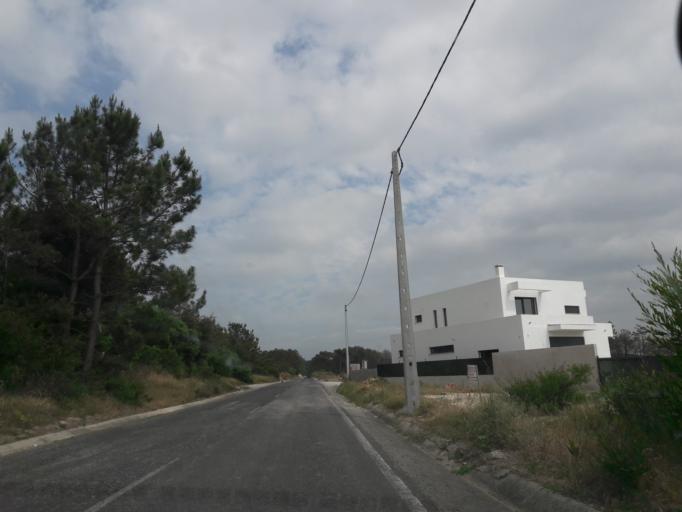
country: PT
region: Leiria
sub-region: Peniche
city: Atouguia da Baleia
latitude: 39.3598
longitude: -9.3053
